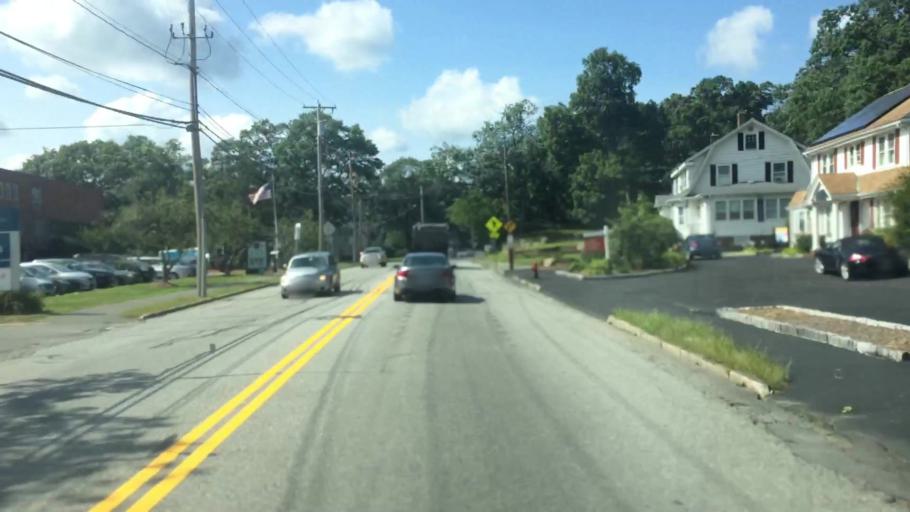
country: US
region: Massachusetts
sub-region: Essex County
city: South Peabody
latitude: 42.5018
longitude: -70.9786
